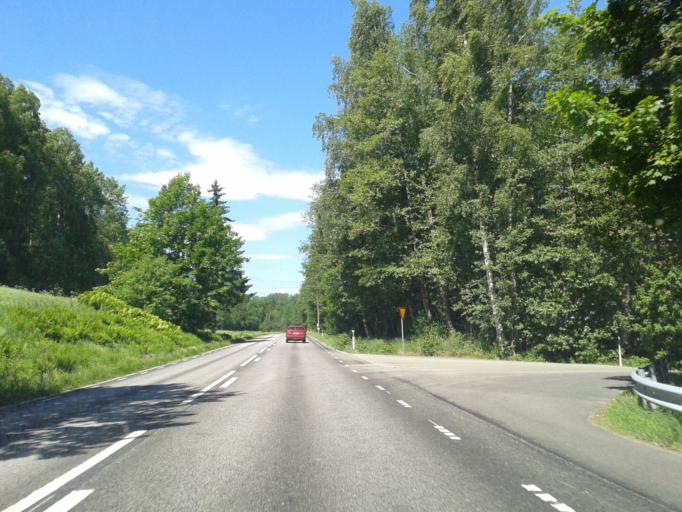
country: SE
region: Vaestra Goetaland
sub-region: Orust
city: Henan
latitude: 58.3174
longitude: 11.6840
